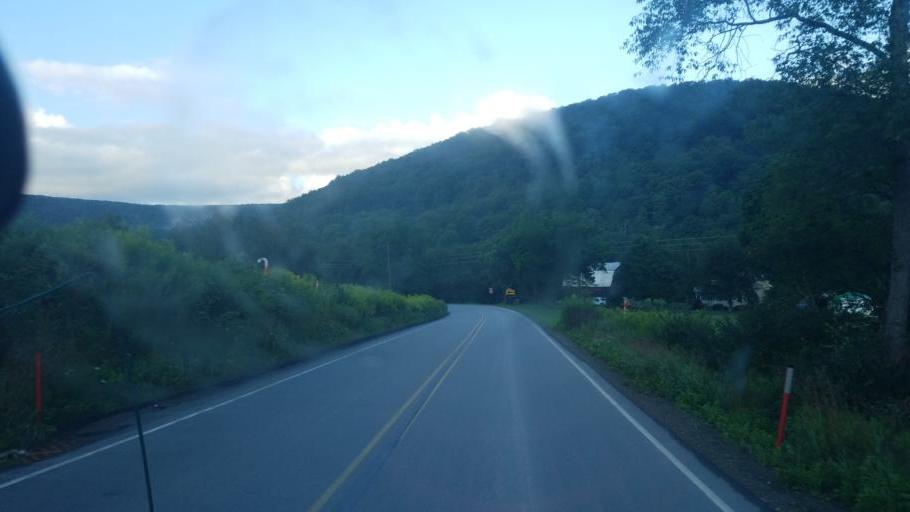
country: US
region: Pennsylvania
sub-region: Potter County
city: Galeton
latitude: 41.8372
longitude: -77.7939
